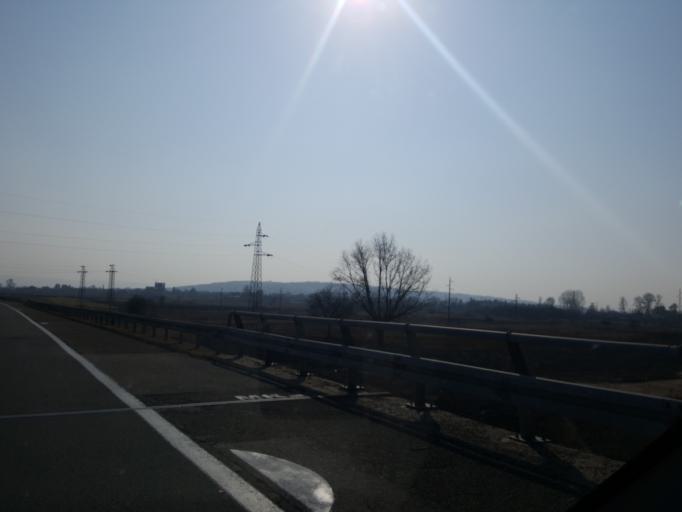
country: RS
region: Central Serbia
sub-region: Nisavski Okrug
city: Doljevac
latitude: 43.2135
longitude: 21.8362
